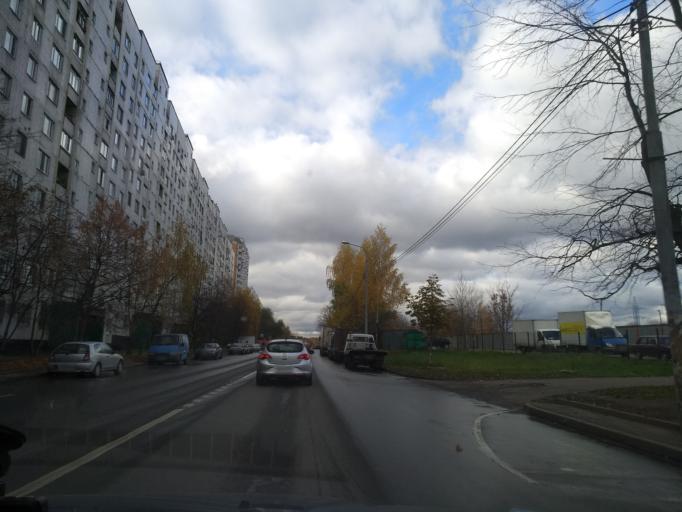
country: RU
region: Moscow
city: Bibirevo
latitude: 55.9003
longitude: 37.6177
